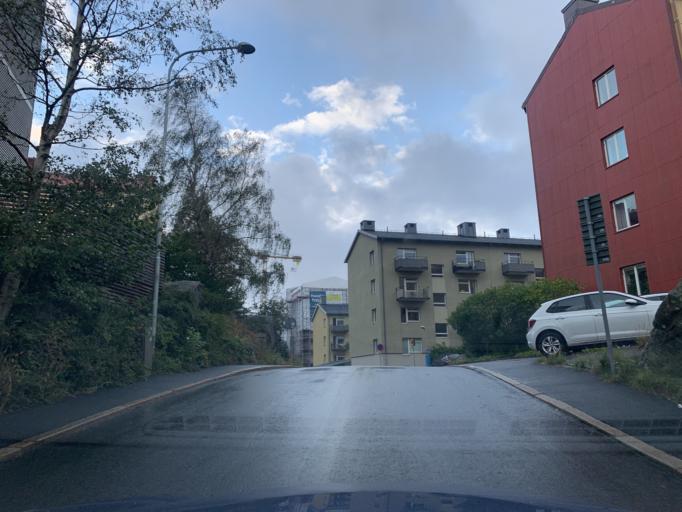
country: SE
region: Vaestra Goetaland
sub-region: Goteborg
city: Goeteborg
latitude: 57.7115
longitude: 12.0125
